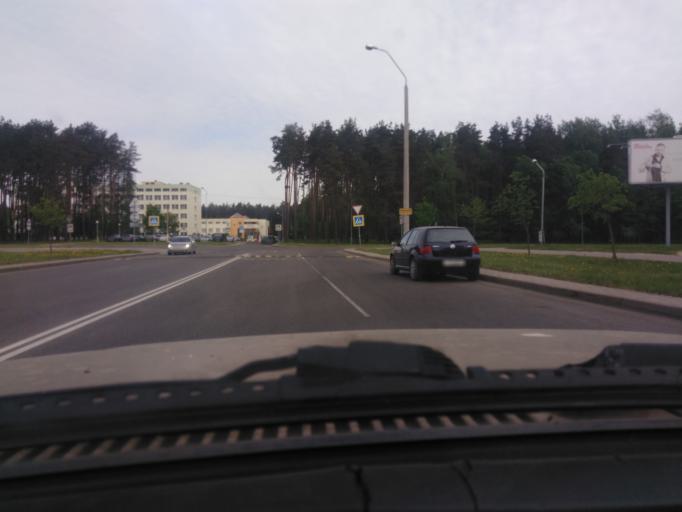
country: BY
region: Mogilev
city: Mahilyow
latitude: 53.9166
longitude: 30.2821
